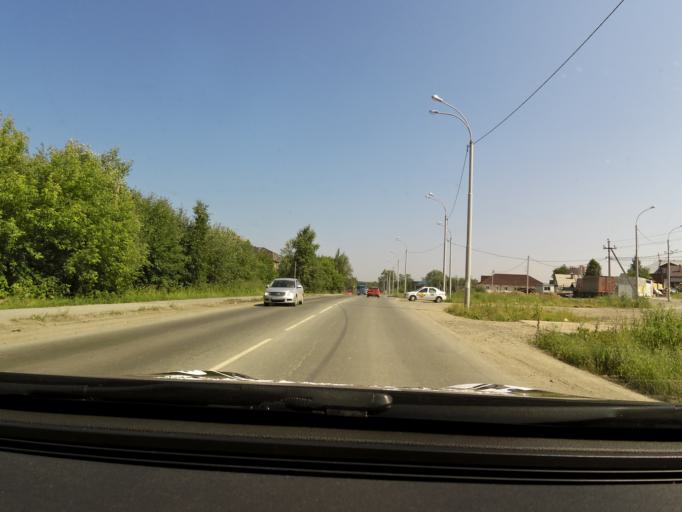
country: RU
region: Sverdlovsk
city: Shirokaya Rechka
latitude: 56.8056
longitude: 60.4950
